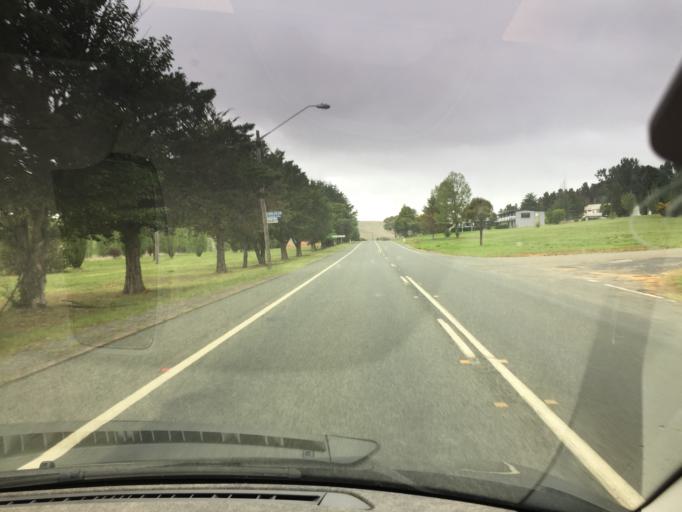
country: AU
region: New South Wales
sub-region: Cooma-Monaro
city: Cooma
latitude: -36.2235
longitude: 149.1343
